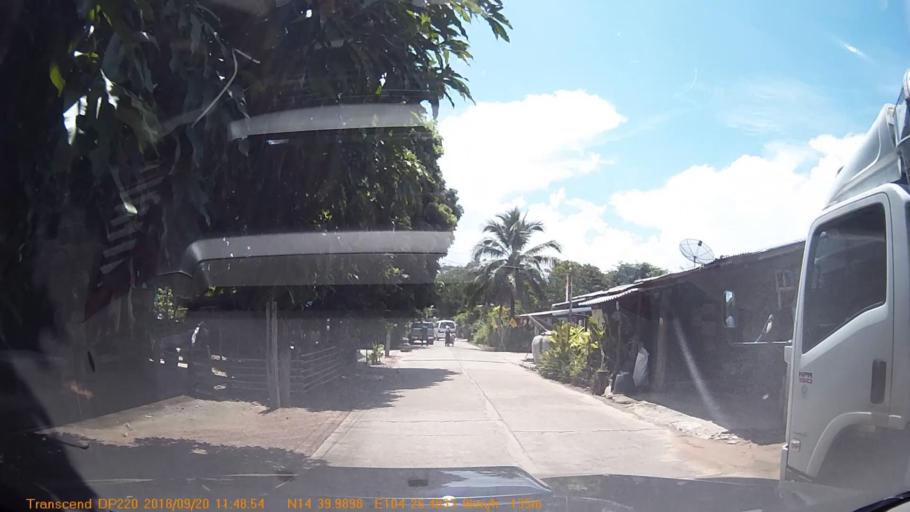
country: TH
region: Sisaket
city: Khun Han
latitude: 14.6665
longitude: 104.4413
